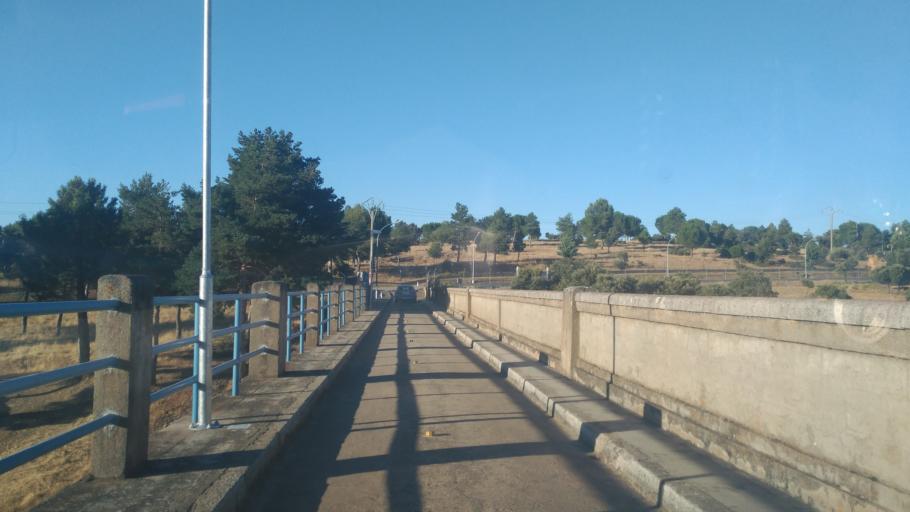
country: ES
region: Castille and Leon
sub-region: Provincia de Salamanca
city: Montejo
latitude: 40.6666
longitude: -5.6096
